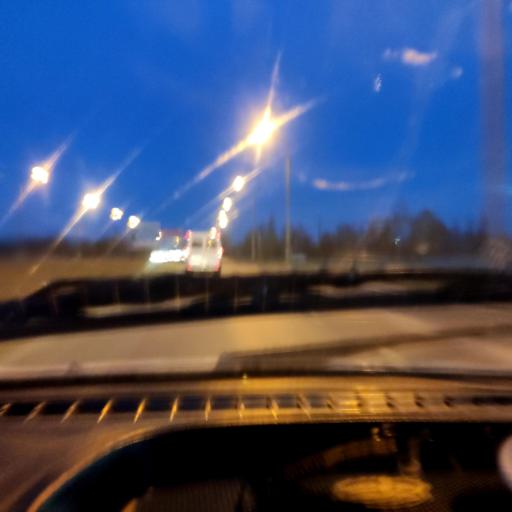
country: RU
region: Samara
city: Tol'yatti
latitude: 53.5575
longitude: 49.3323
